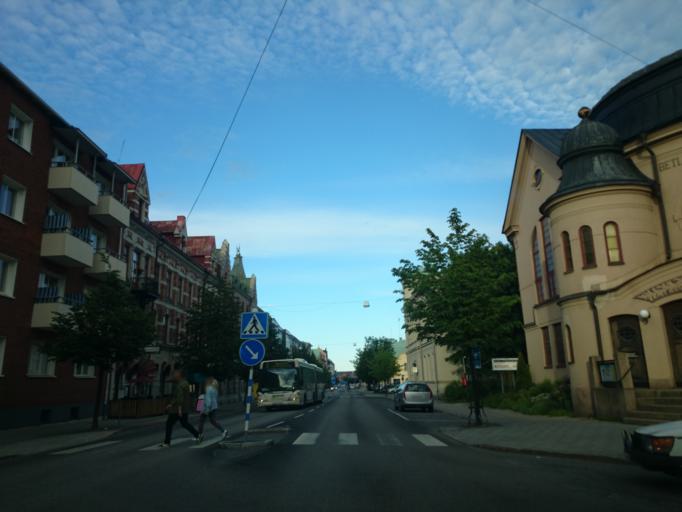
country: SE
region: Vaesternorrland
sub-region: Sundsvalls Kommun
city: Sundsvall
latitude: 62.3892
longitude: 17.3036
